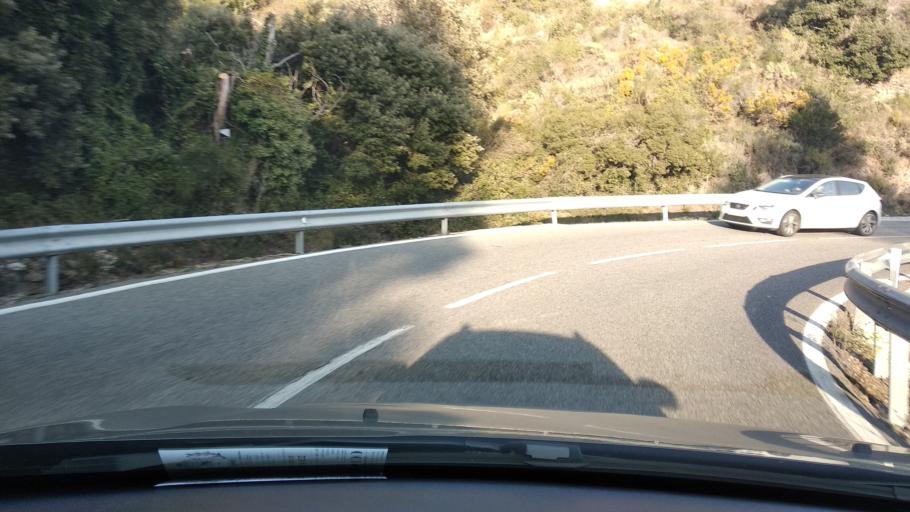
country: ES
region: Catalonia
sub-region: Provincia de Tarragona
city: Alforja
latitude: 41.2201
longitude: 0.9500
